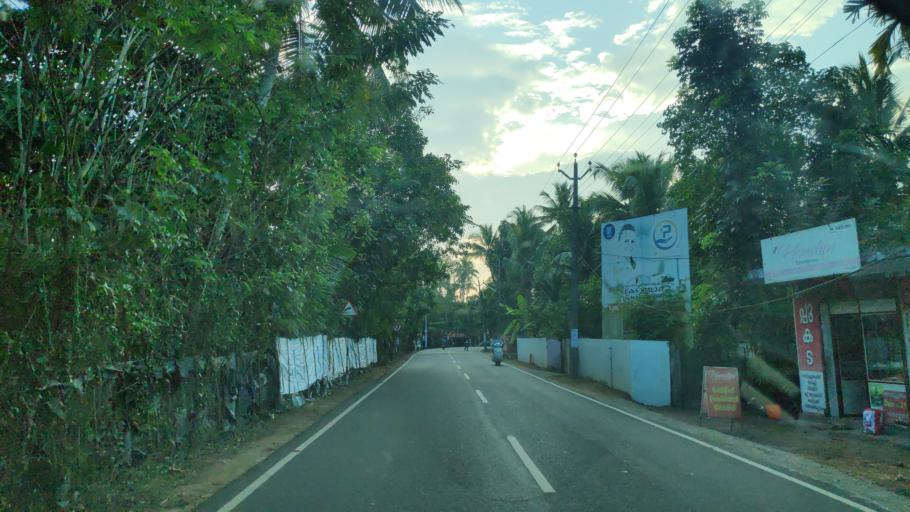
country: IN
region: Kerala
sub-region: Alappuzha
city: Shertallai
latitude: 9.6762
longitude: 76.3839
